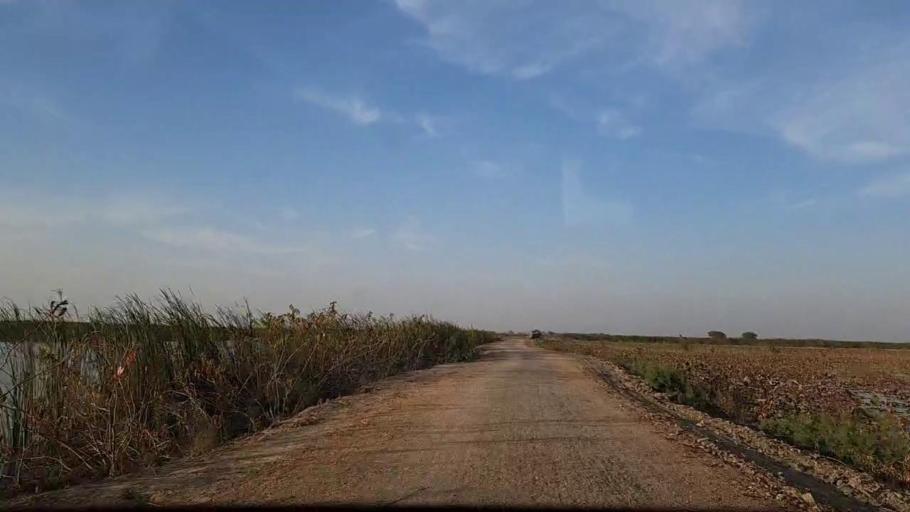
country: PK
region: Sindh
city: Mirpur Batoro
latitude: 24.6556
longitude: 68.1465
